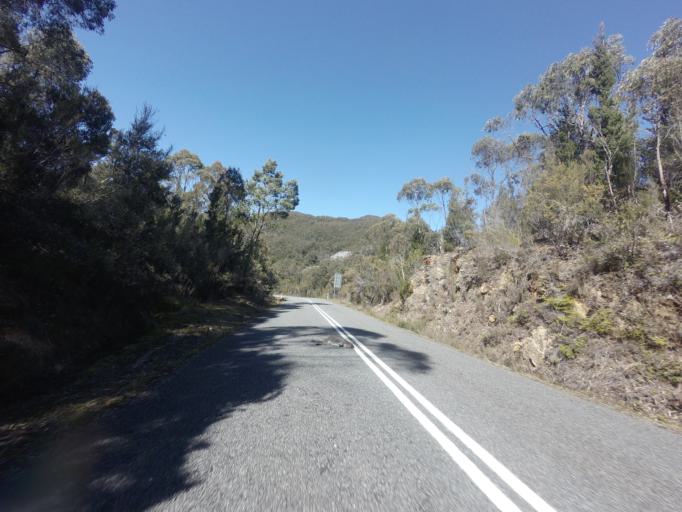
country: AU
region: Tasmania
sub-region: Huon Valley
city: Geeveston
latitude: -42.8145
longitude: 146.3832
